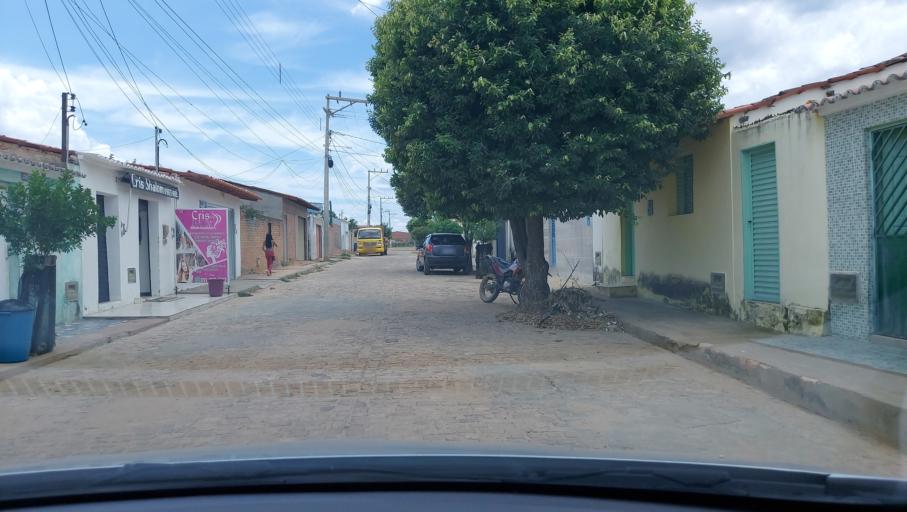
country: BR
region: Bahia
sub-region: Oliveira Dos Brejinhos
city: Beira Rio
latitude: -11.9992
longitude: -42.6304
